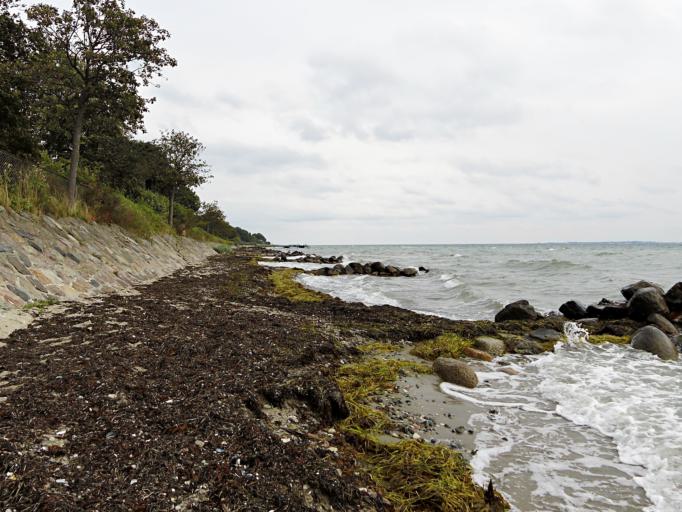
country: DK
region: Capital Region
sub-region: Rudersdal Kommune
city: Trorod
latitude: 55.8300
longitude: 12.5745
